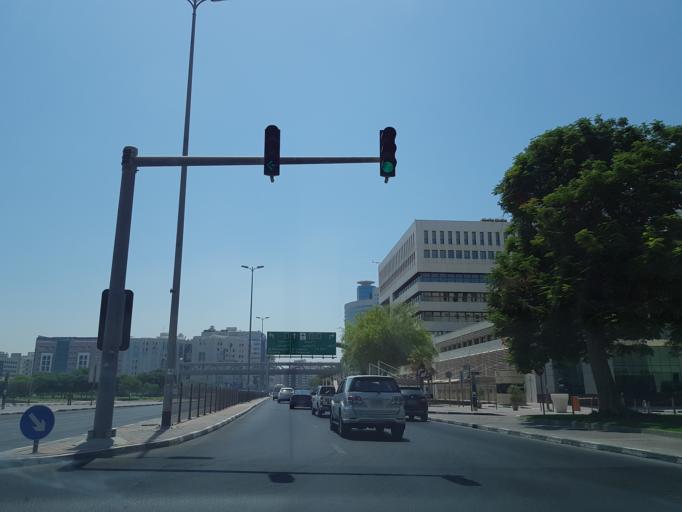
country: AE
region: Ash Shariqah
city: Sharjah
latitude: 25.2657
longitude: 55.3114
